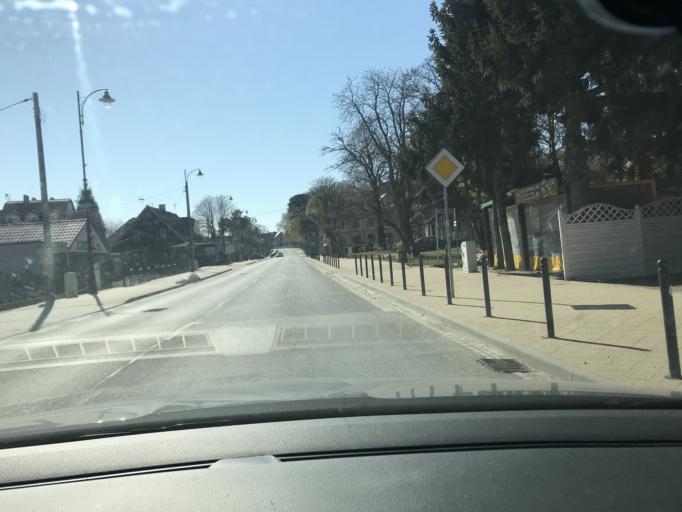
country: PL
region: Pomeranian Voivodeship
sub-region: Powiat nowodworski
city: Krynica Morska
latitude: 54.3788
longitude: 19.4406
